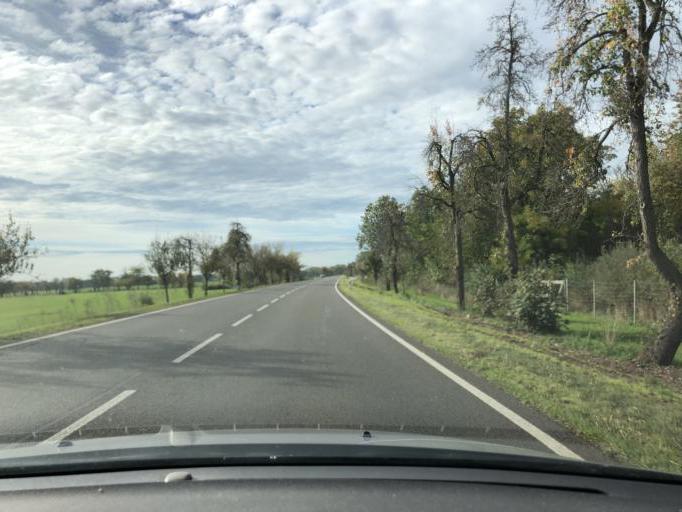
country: DE
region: Saxony
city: Elstertrebnitz
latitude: 51.1480
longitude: 12.2451
